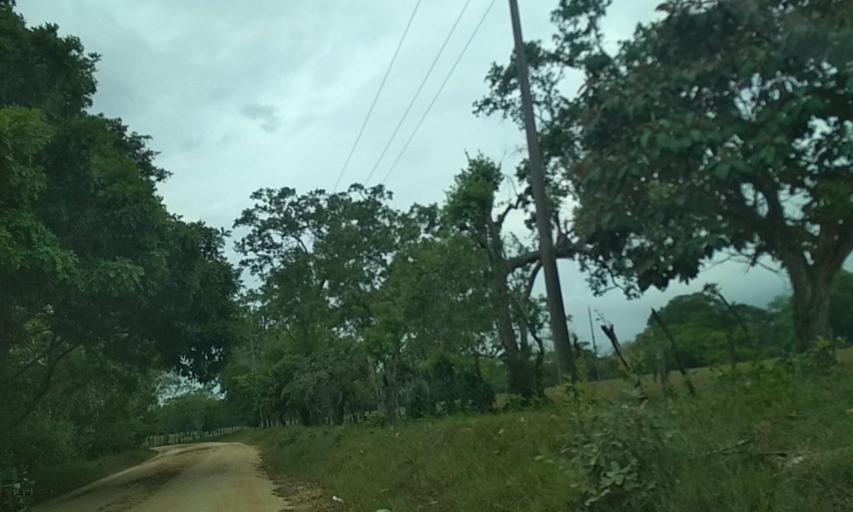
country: MX
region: Veracruz
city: Las Choapas
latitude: 17.8893
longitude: -94.1221
